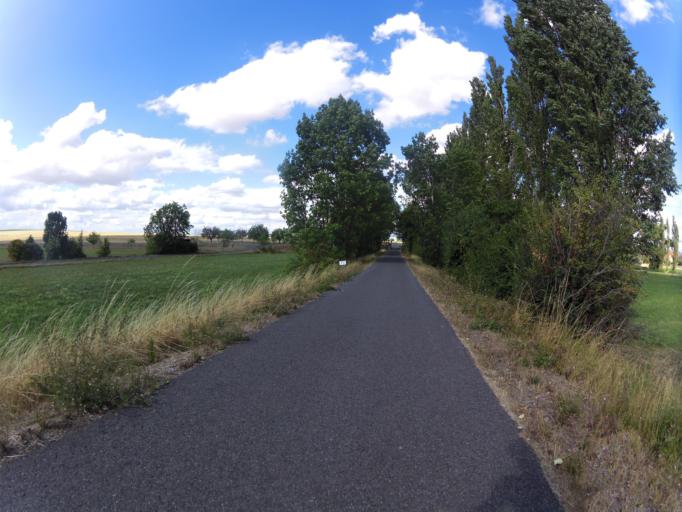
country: DE
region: Bavaria
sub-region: Regierungsbezirk Unterfranken
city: Sonderhofen
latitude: 49.6096
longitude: 10.0074
